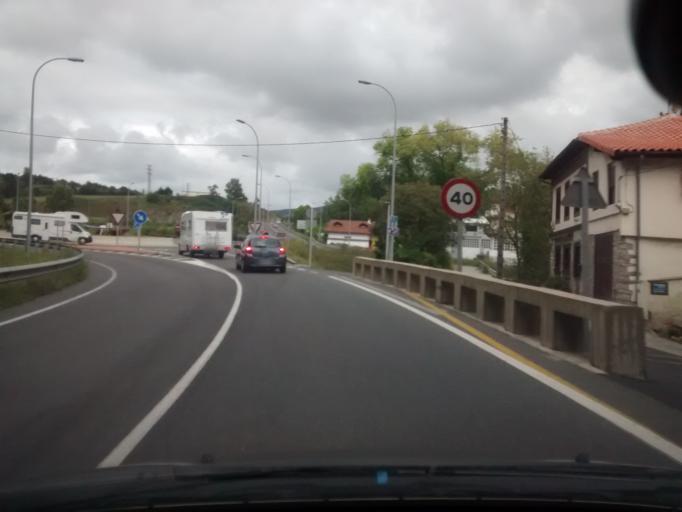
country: ES
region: Basque Country
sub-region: Provincia de Guipuzcoa
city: Zumaia
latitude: 43.2851
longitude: -2.2607
